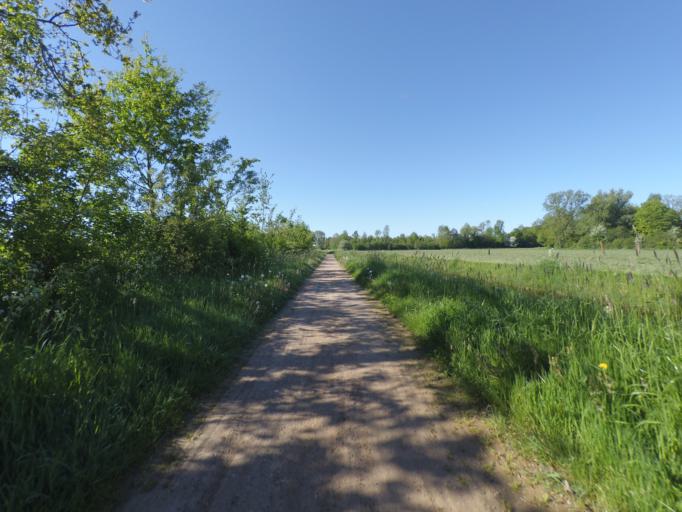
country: NL
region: Gelderland
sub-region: Gemeente Voorst
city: Wilp
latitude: 52.2097
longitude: 6.1233
